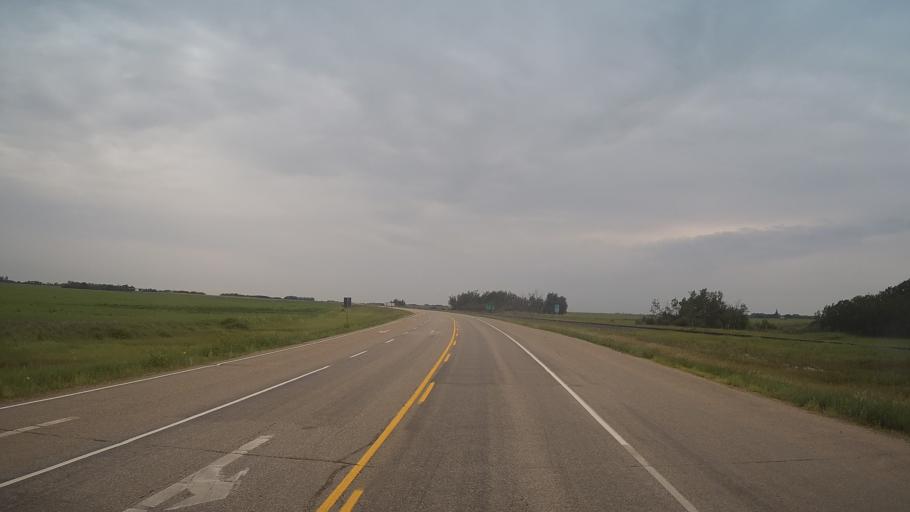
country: CA
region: Saskatchewan
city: Langham
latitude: 52.1260
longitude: -107.2890
